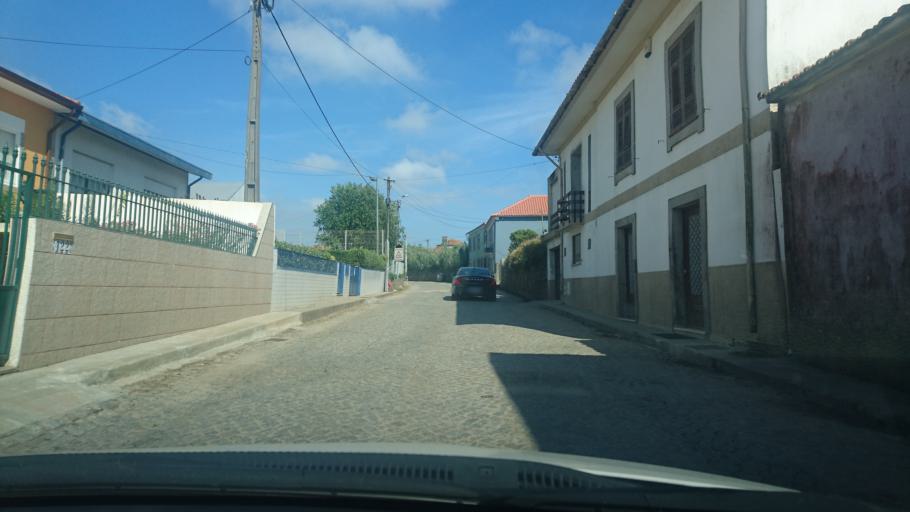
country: PT
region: Porto
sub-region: Matosinhos
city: Lavra
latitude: 41.2678
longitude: -8.7134
